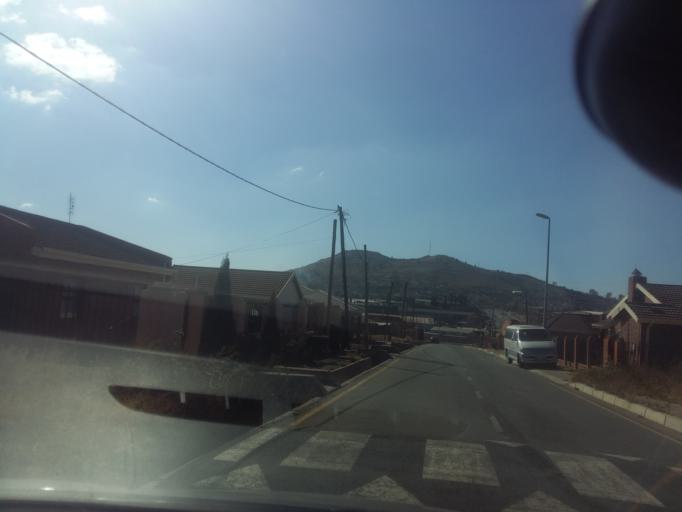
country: LS
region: Maseru
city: Maseru
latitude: -29.3451
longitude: 27.4555
